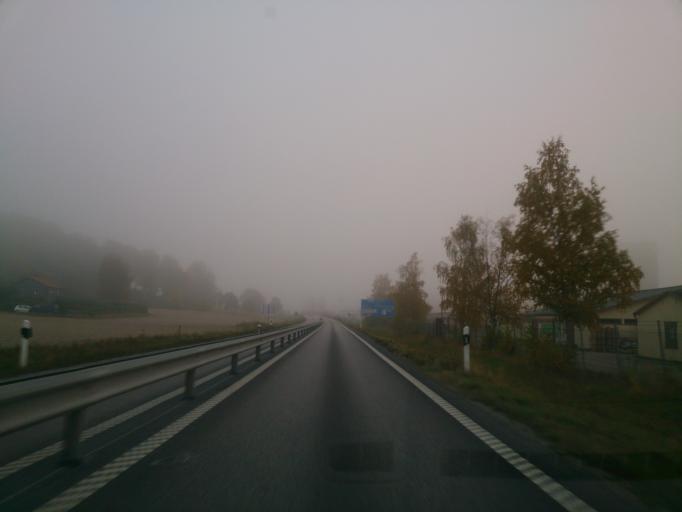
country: SE
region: OEstergoetland
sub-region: Kinda Kommun
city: Rimforsa
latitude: 58.1349
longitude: 15.6787
